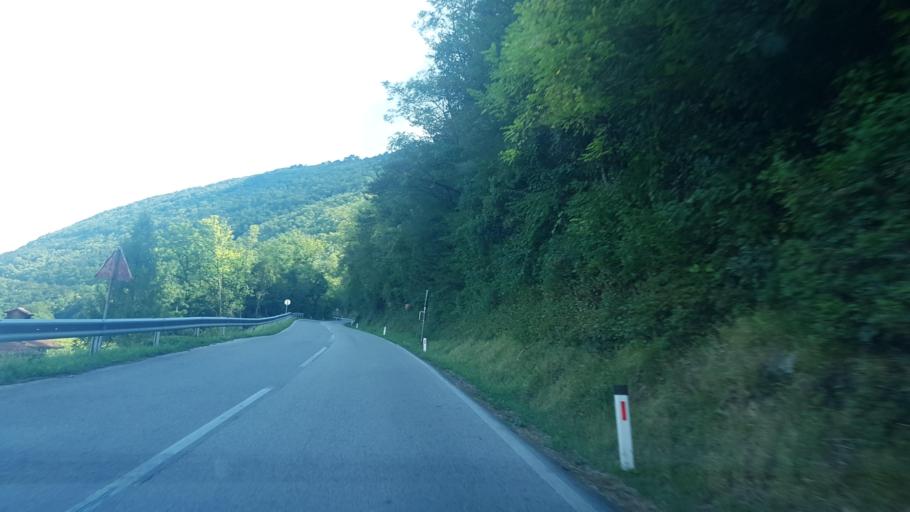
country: SI
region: Komen
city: Komen
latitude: 45.8506
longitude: 13.8039
